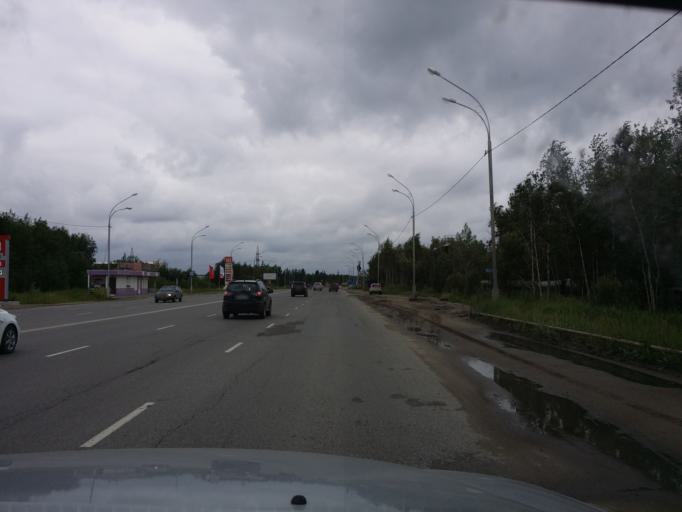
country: RU
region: Khanty-Mansiyskiy Avtonomnyy Okrug
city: Nizhnevartovsk
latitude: 60.9643
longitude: 76.5308
